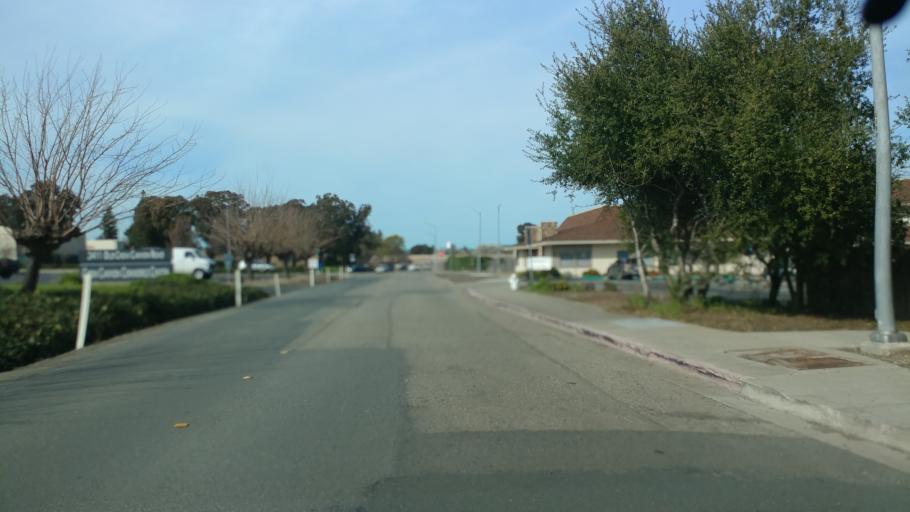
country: US
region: California
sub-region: Contra Costa County
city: San Ramon
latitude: 37.7788
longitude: -121.9796
